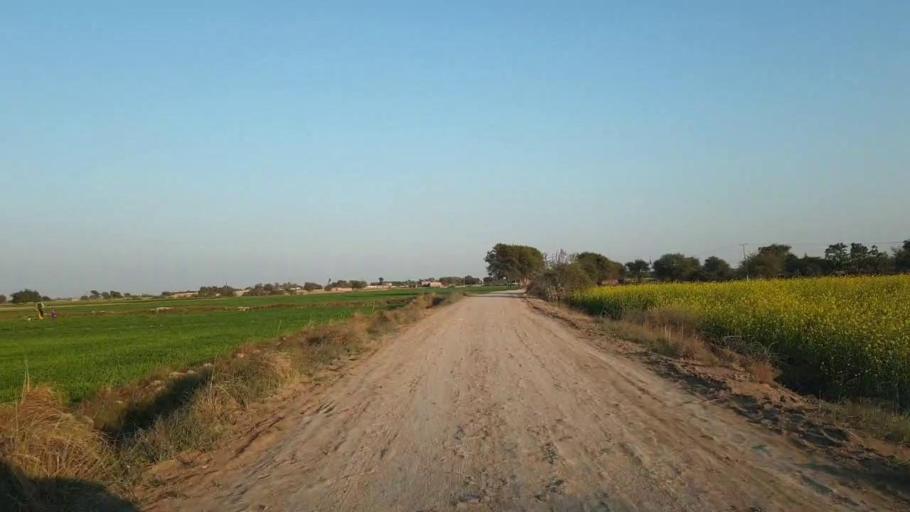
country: PK
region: Sindh
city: Shahpur Chakar
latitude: 26.1526
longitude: 68.5609
